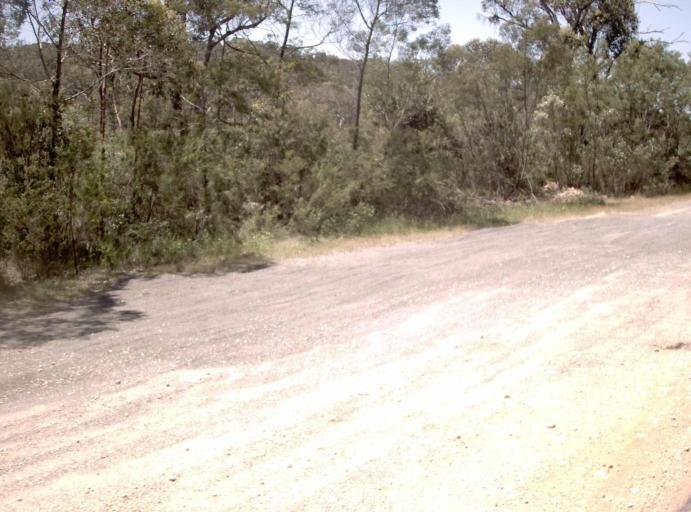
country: AU
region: Victoria
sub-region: East Gippsland
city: Lakes Entrance
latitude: -37.7115
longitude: 148.6721
